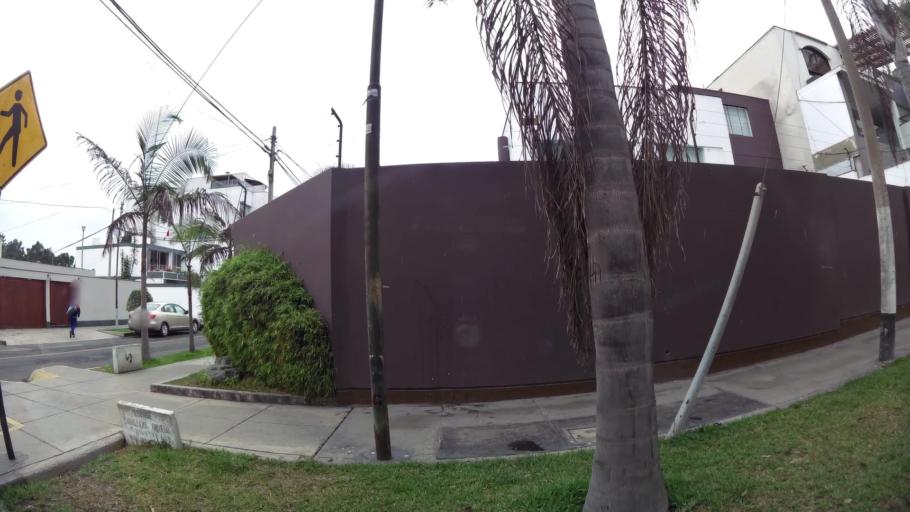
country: PE
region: Lima
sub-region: Lima
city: Surco
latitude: -12.1256
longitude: -77.0057
